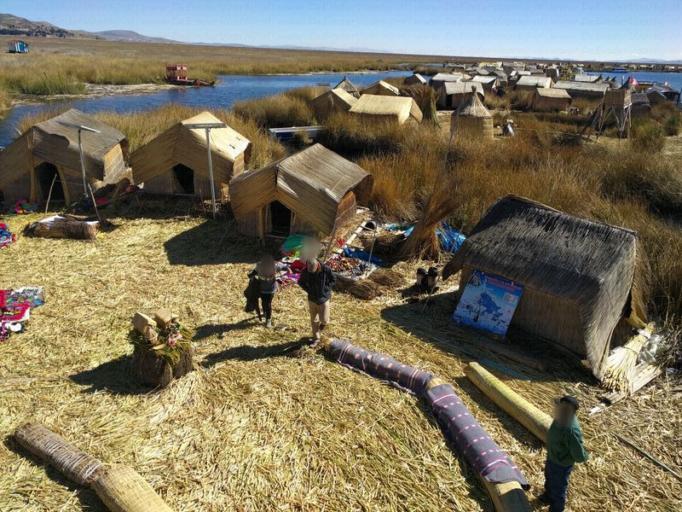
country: PE
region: Puno
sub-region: Provincia de Puno
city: Puno
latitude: -15.8137
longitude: -69.9749
